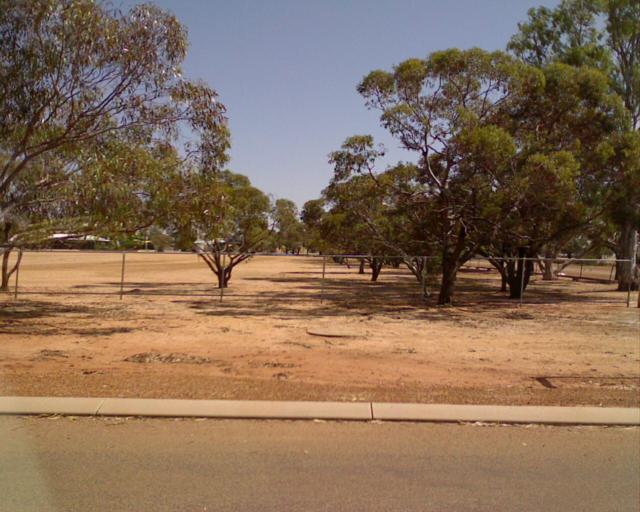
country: AU
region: Western Australia
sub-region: Merredin
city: Merredin
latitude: -30.9191
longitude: 118.2093
